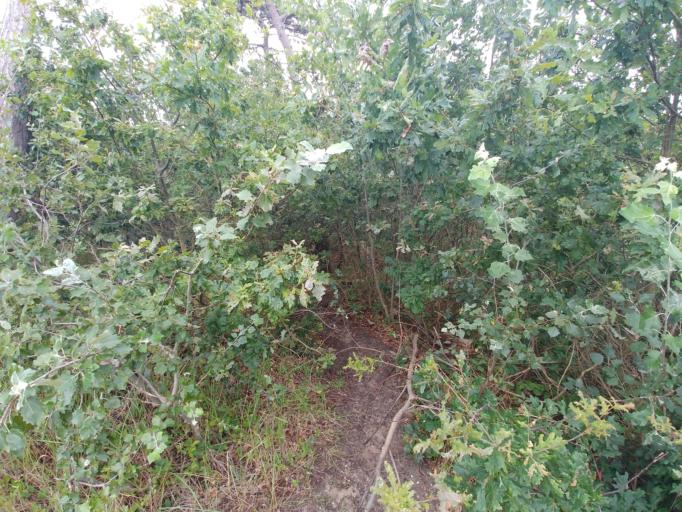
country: NL
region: North Holland
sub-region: Gemeente Alkmaar
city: Alkmaar
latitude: 52.6837
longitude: 4.6952
